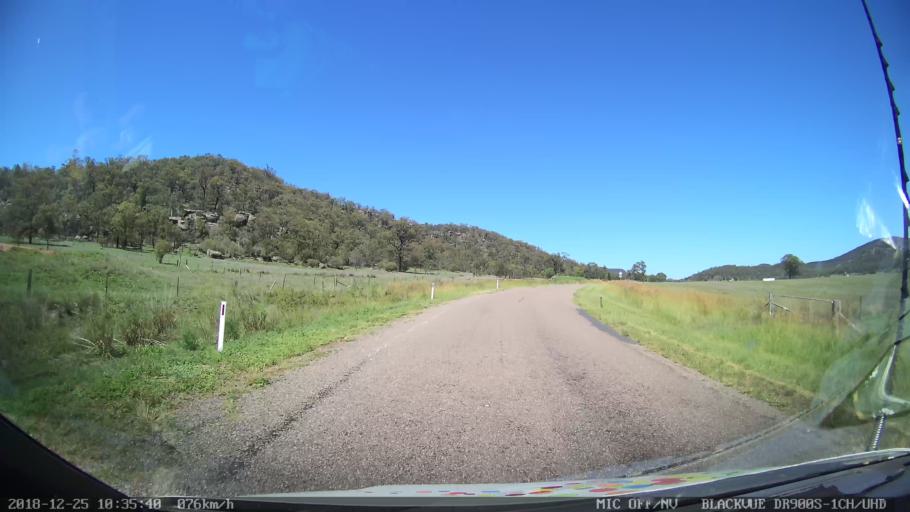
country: AU
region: New South Wales
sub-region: Upper Hunter Shire
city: Merriwa
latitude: -32.4012
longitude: 150.3944
